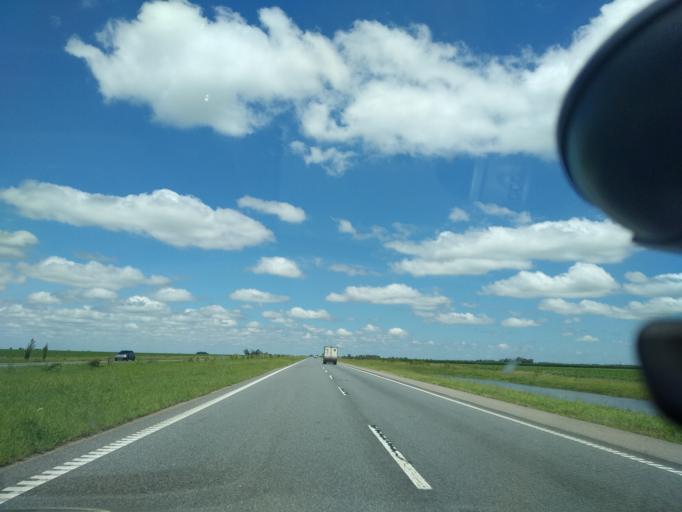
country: AR
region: Cordoba
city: Oliva
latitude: -31.9586
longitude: -63.5918
